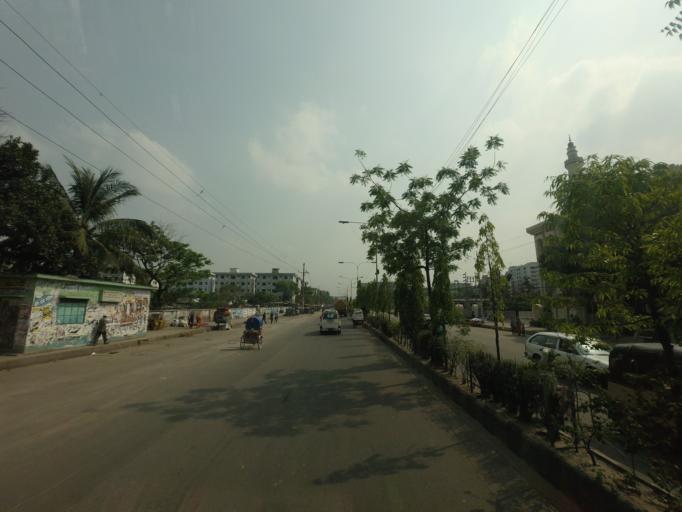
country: BD
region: Dhaka
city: Azimpur
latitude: 23.7932
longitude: 90.3537
